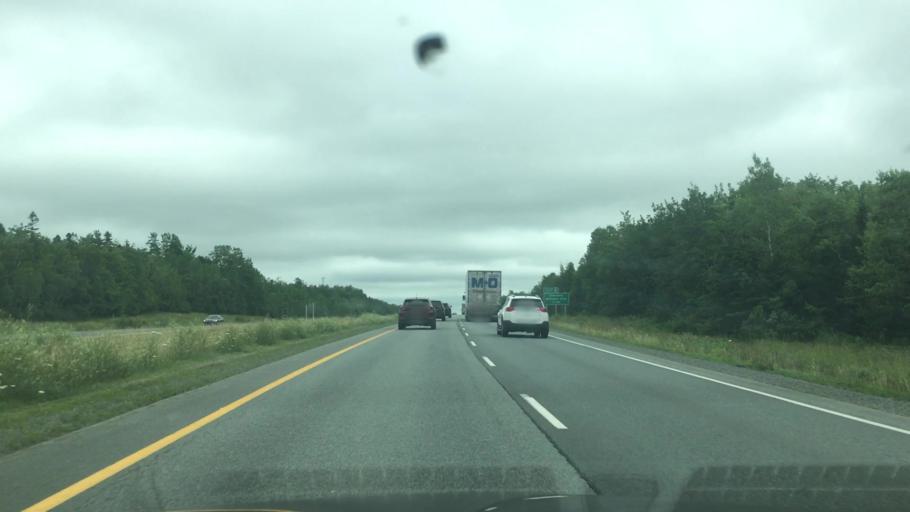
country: CA
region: Nova Scotia
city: Dartmouth
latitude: 44.9581
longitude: -63.5354
